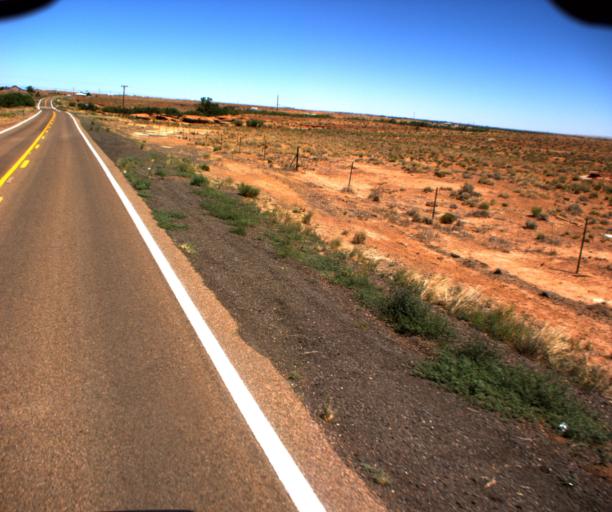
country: US
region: Arizona
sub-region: Navajo County
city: Winslow
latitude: 34.9740
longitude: -110.6509
